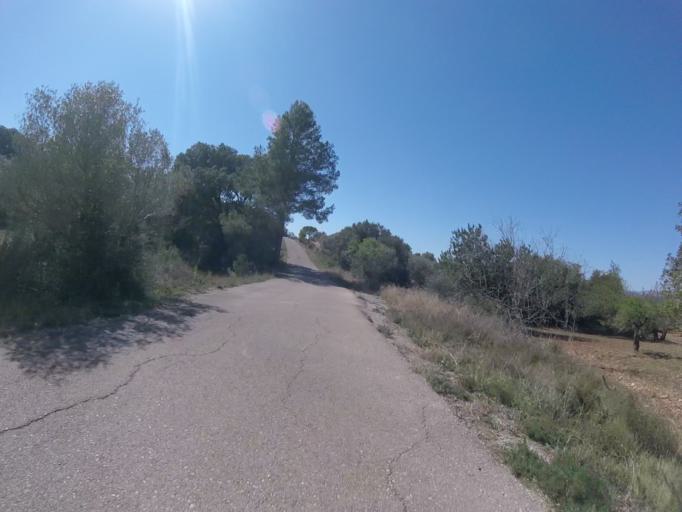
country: ES
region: Valencia
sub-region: Provincia de Castello
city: Cuevas de Vinroma
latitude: 40.3829
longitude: 0.1559
